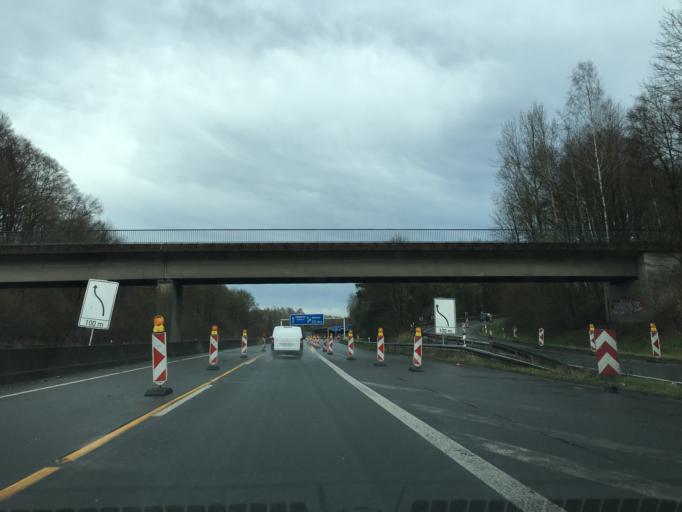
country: DE
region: North Rhine-Westphalia
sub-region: Regierungsbezirk Munster
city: Haltern
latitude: 51.7022
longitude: 7.1435
